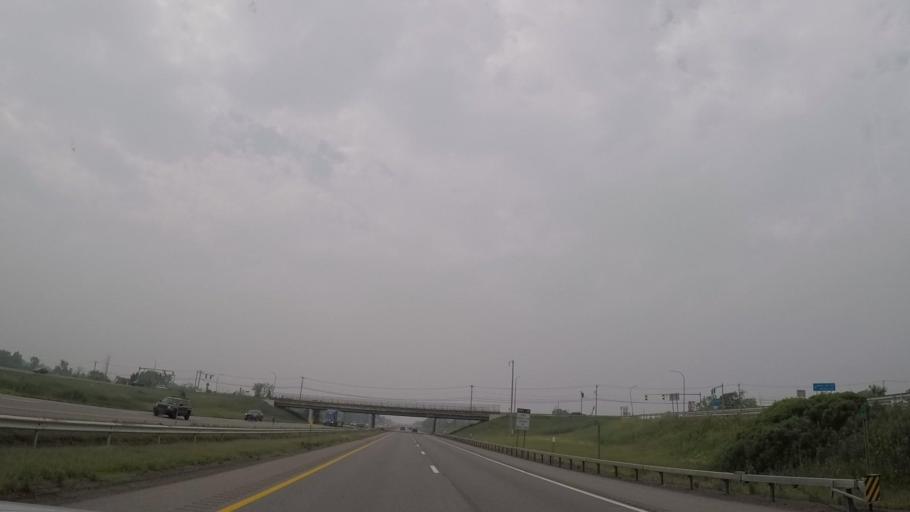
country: US
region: New York
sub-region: Erie County
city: Grandyle Village
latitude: 43.0204
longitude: -78.9736
